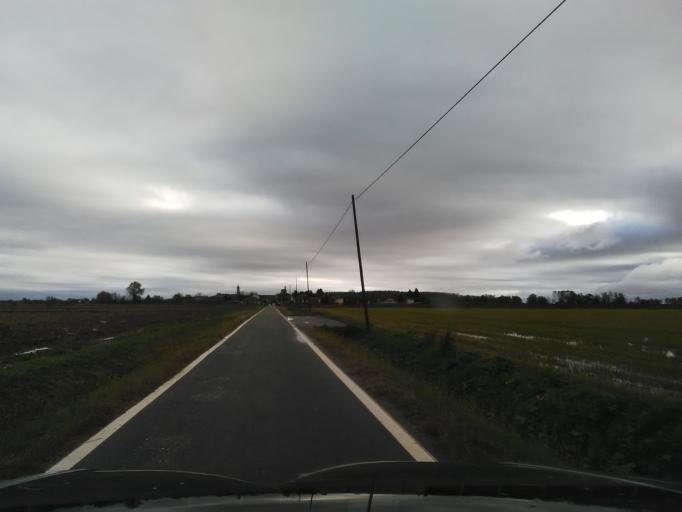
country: IT
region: Piedmont
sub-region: Provincia di Vercelli
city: Casanova Elvo
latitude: 45.4012
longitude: 8.2835
